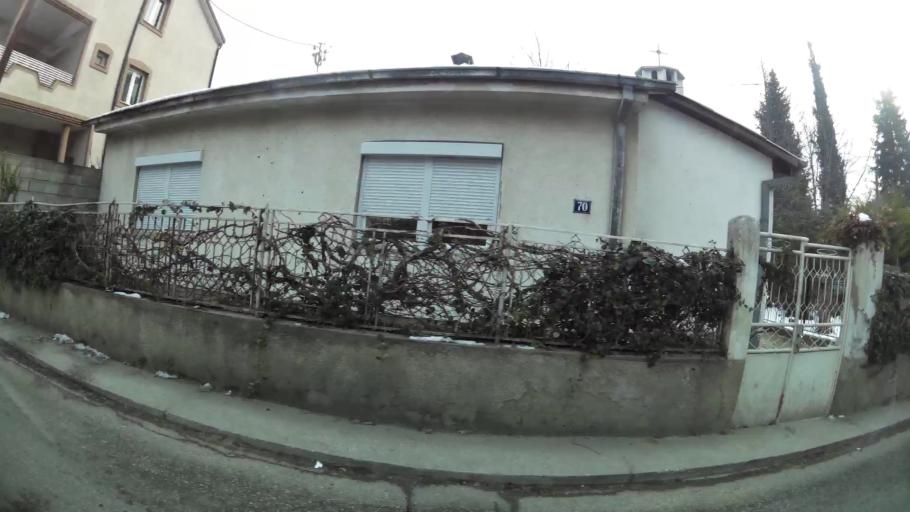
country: MK
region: Cair
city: Cair
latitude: 42.0123
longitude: 21.4433
